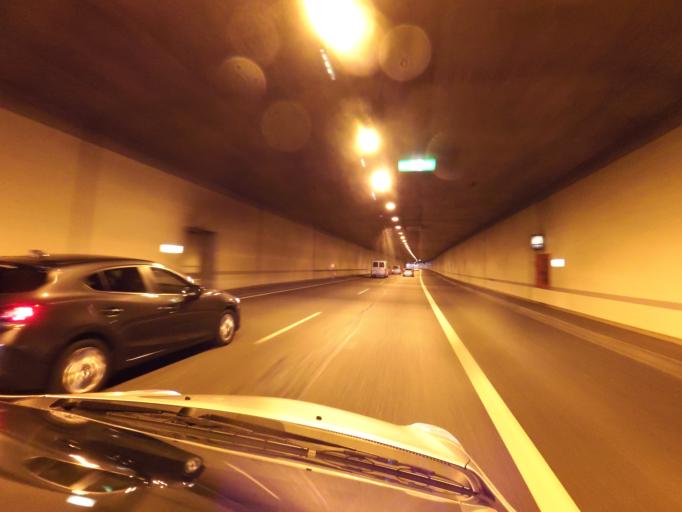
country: DE
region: Baden-Wuerttemberg
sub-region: Karlsruhe Region
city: Karlsruhe
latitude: 48.9912
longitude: 8.3860
